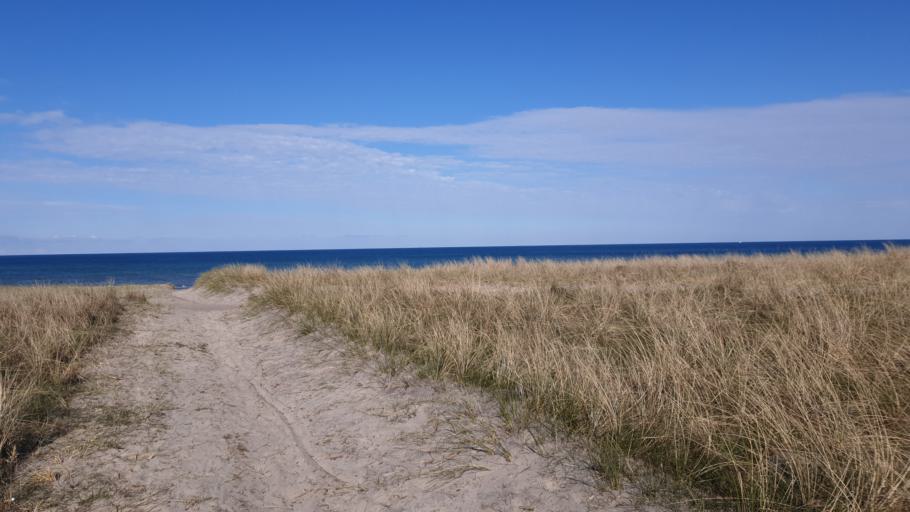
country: DK
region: North Denmark
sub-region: Hjorring Kommune
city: Hjorring
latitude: 57.4945
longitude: 9.8308
